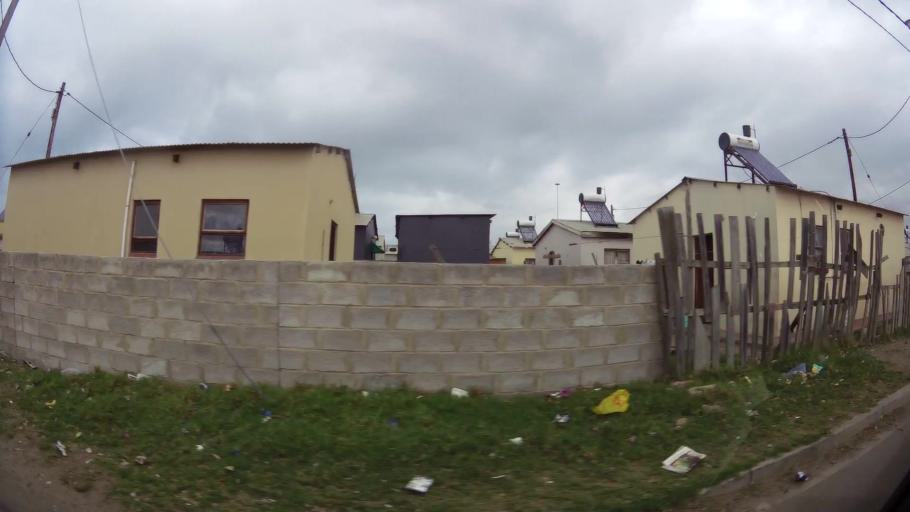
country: ZA
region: Eastern Cape
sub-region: Nelson Mandela Bay Metropolitan Municipality
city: Port Elizabeth
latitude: -33.8884
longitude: 25.6021
